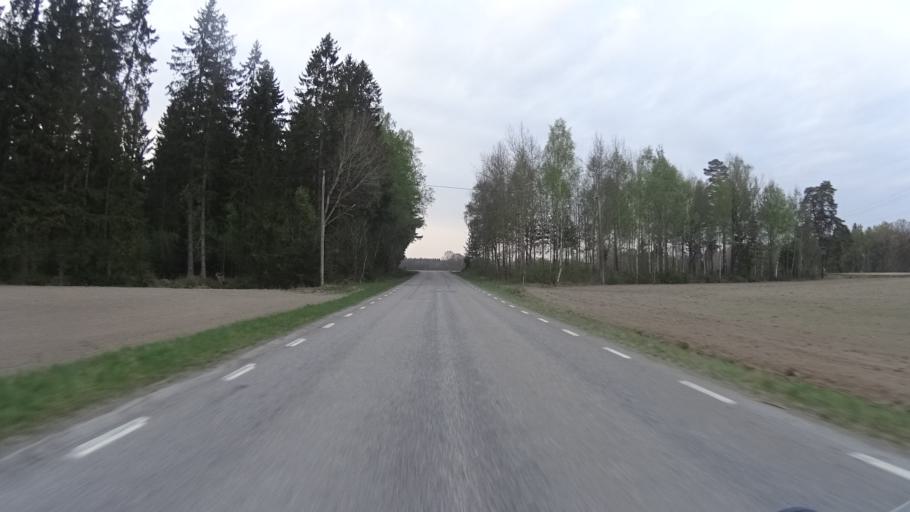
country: SE
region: Vaestra Goetaland
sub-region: Lidkopings Kommun
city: Vinninga
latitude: 58.4355
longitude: 13.3388
